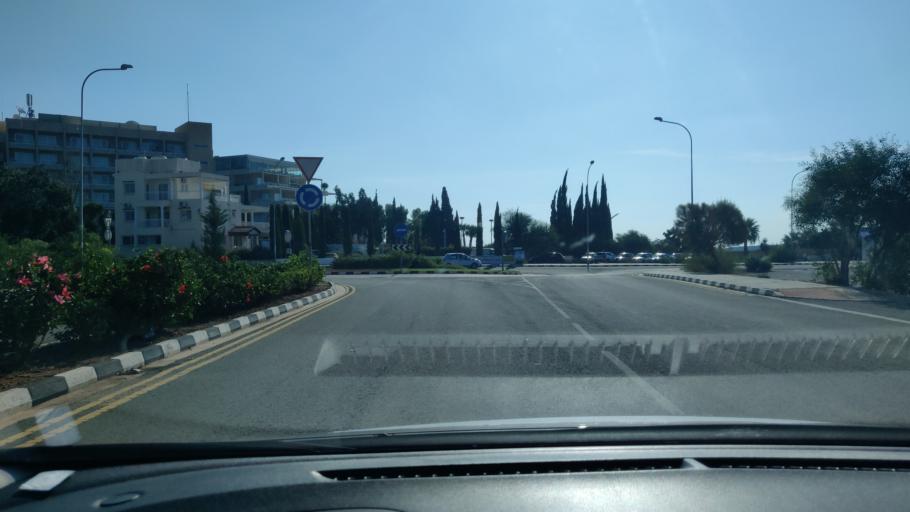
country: CY
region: Ammochostos
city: Protaras
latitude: 34.9857
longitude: 34.0664
